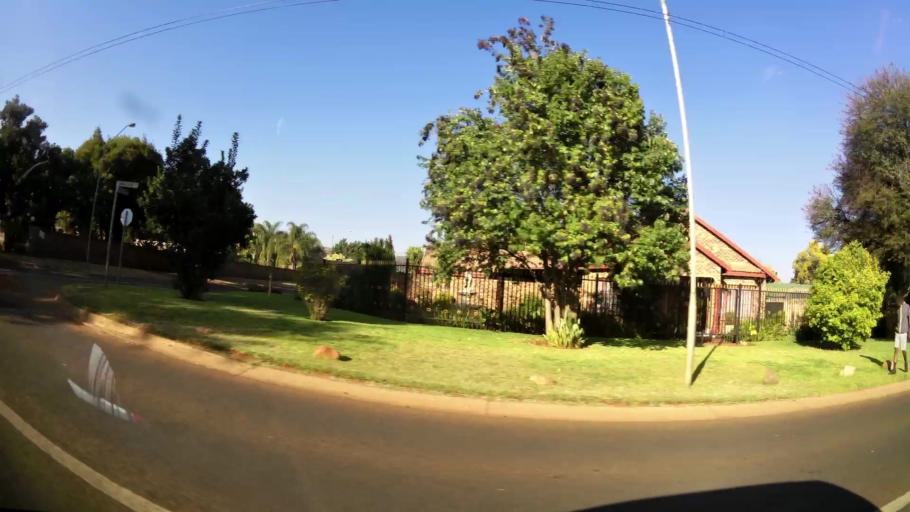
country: ZA
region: Gauteng
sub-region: City of Tshwane Metropolitan Municipality
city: Pretoria
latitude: -25.6721
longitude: 28.2057
